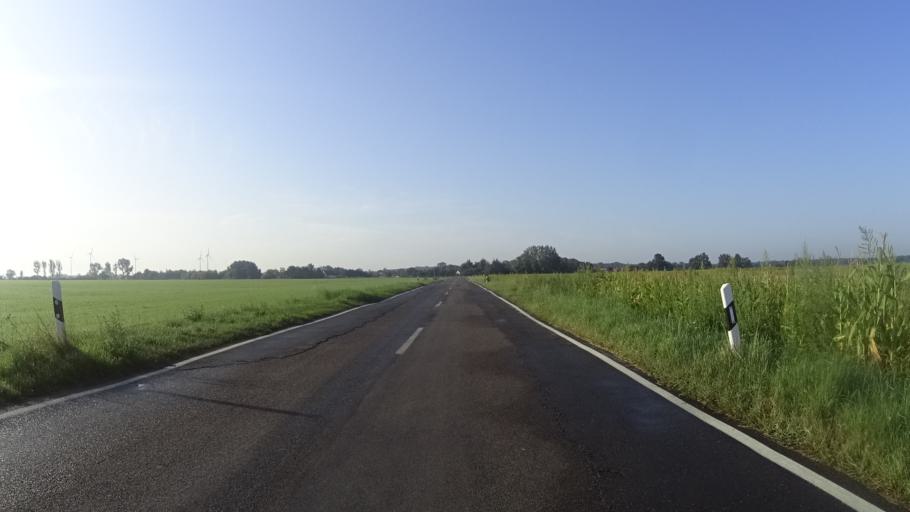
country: DE
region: Brandenburg
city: Kasel-Golzig
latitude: 51.9961
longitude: 13.6914
